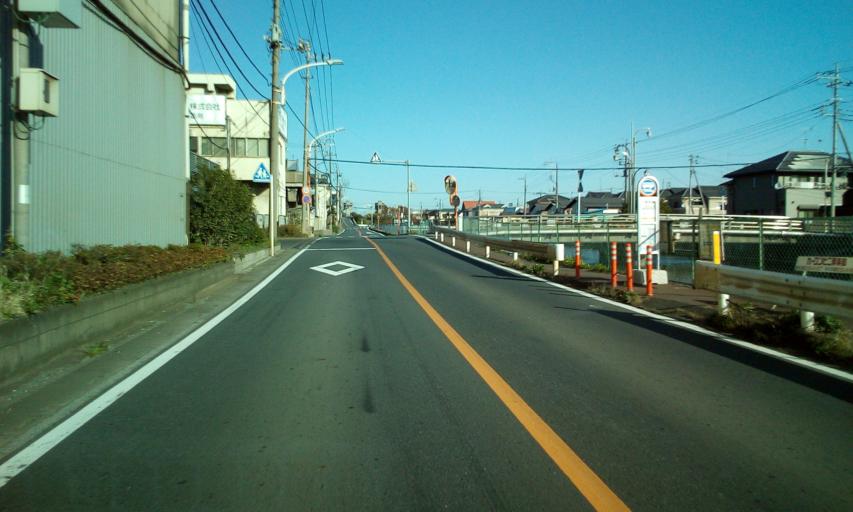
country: JP
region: Chiba
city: Matsudo
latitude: 35.8147
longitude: 139.8837
